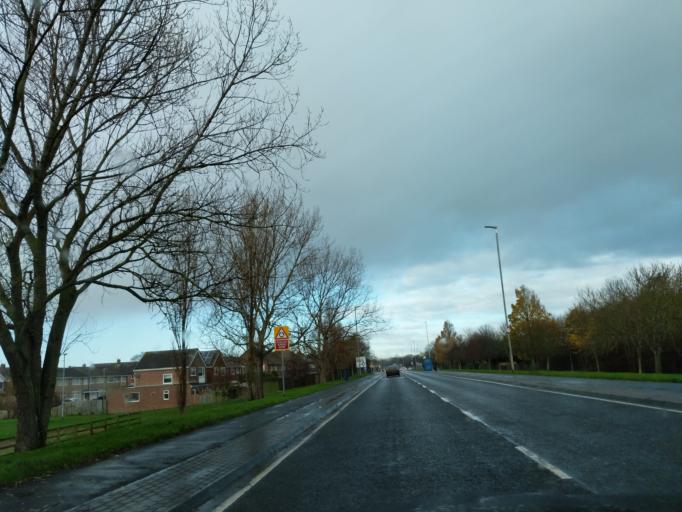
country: GB
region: England
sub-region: Northumberland
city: Blyth
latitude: 55.1171
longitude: -1.5090
